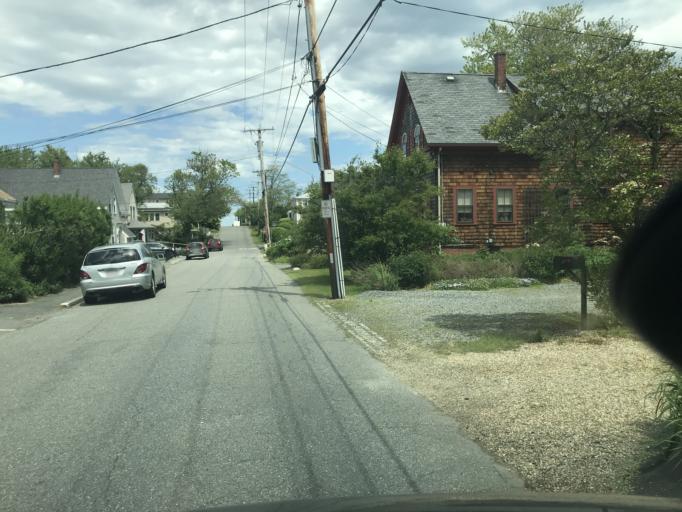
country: US
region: Massachusetts
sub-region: Essex County
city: Rockport
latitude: 42.6575
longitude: -70.6127
